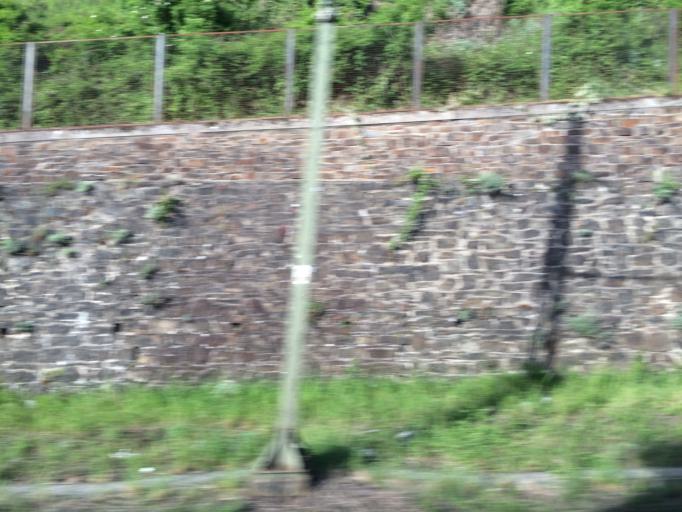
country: DE
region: Rheinland-Pfalz
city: Sankt Goar
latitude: 50.1539
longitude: 7.7187
